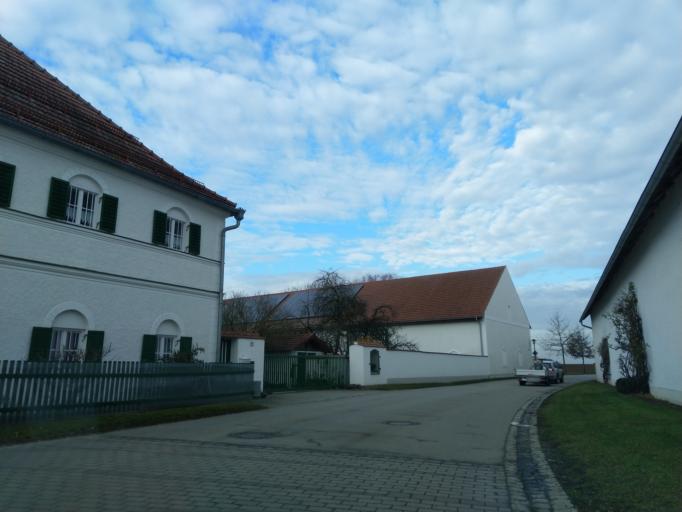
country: DE
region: Bavaria
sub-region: Lower Bavaria
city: Buchhofen
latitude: 48.7160
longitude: 12.9412
